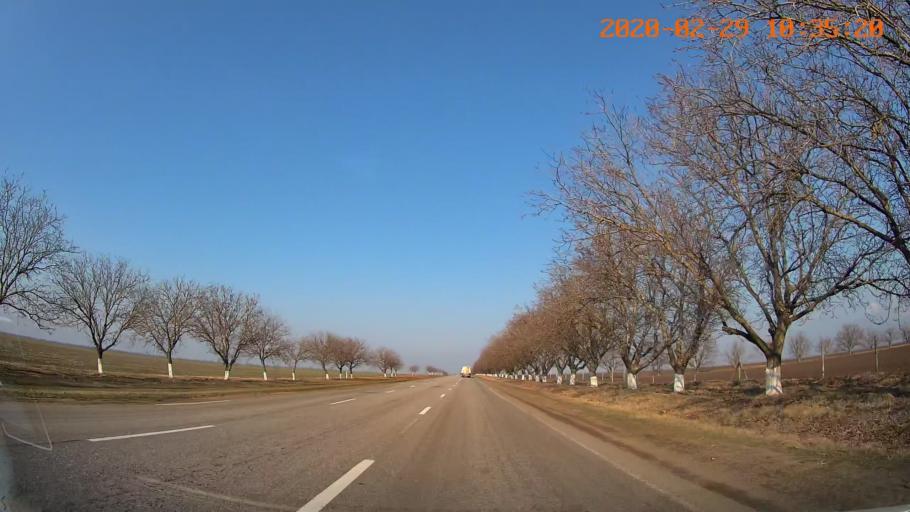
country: MD
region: Anenii Noi
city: Varnita
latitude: 46.9847
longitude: 29.5220
